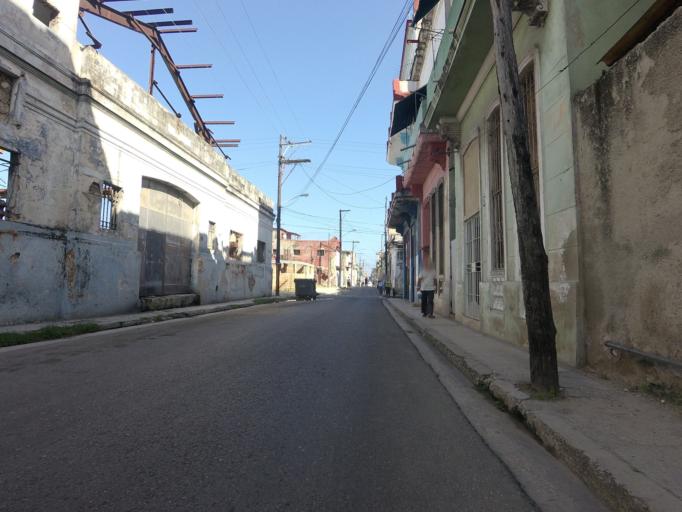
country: CU
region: La Habana
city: Cerro
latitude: 23.1172
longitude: -82.3726
